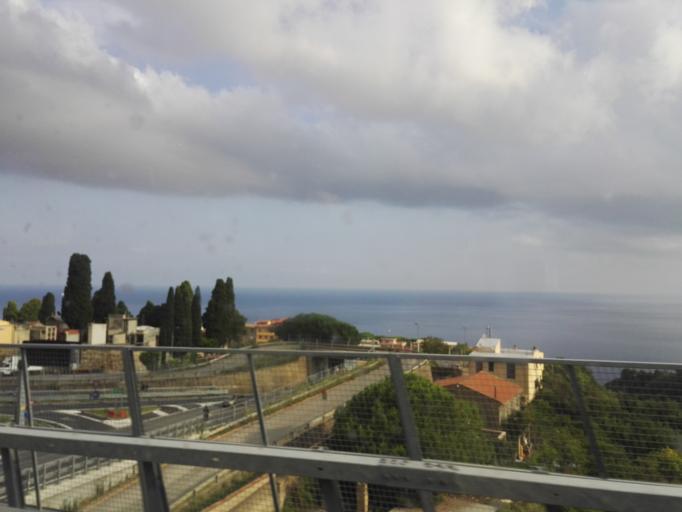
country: IT
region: Calabria
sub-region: Provincia di Reggio Calabria
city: Scilla
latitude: 38.2487
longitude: 15.7222
